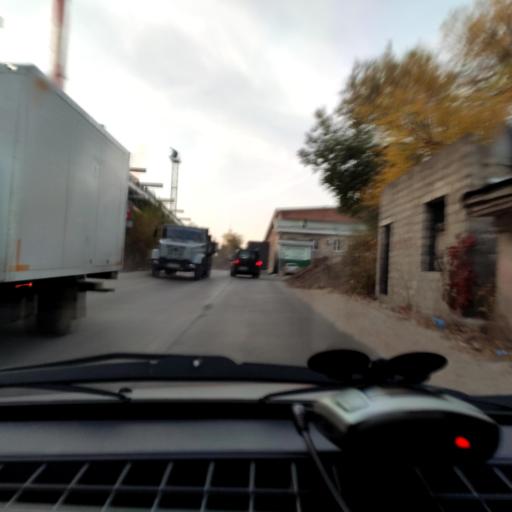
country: RU
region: Voronezj
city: Voronezh
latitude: 51.6881
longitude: 39.1545
